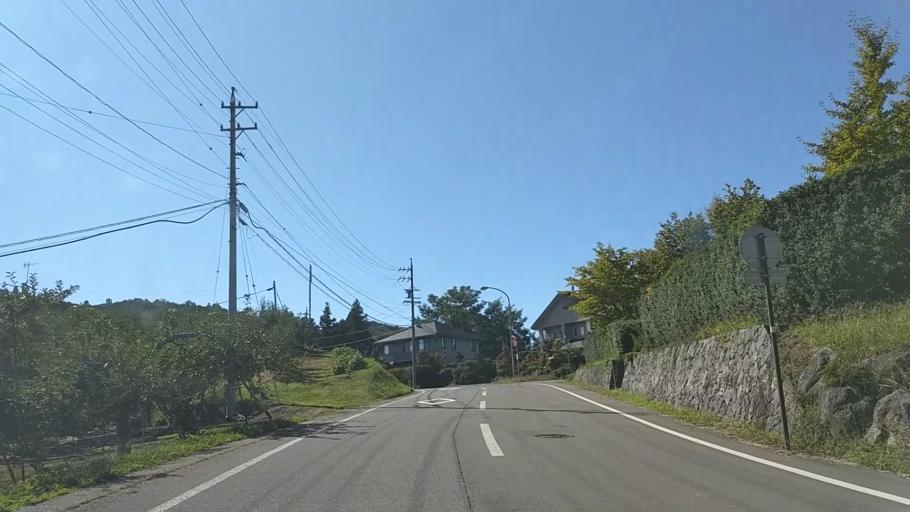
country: JP
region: Nagano
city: Nagano-shi
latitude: 36.5850
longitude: 138.1118
